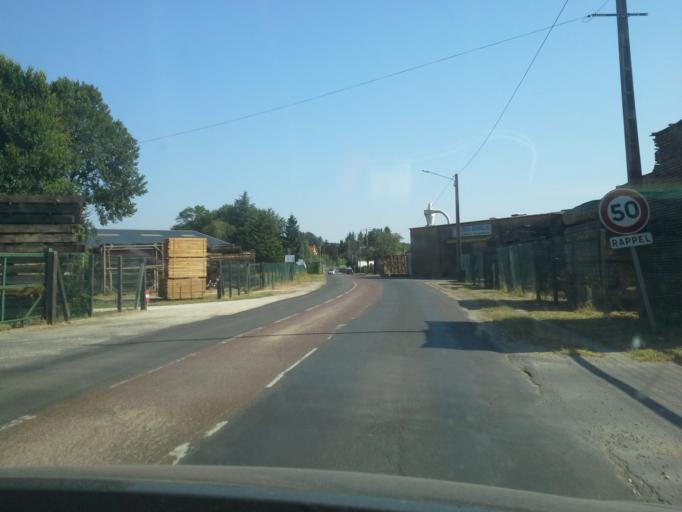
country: FR
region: Centre
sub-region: Departement du Loir-et-Cher
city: Les Montils
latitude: 47.5194
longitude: 1.3008
